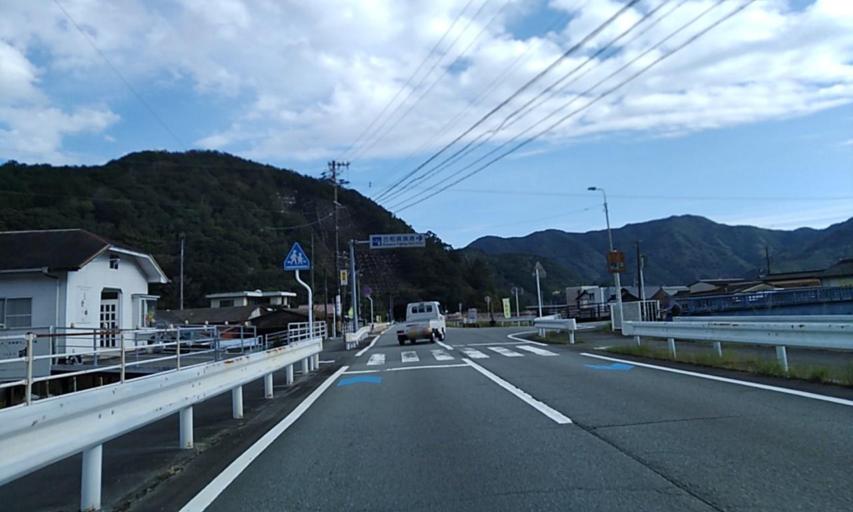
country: JP
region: Mie
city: Owase
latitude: 34.2578
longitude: 136.4603
